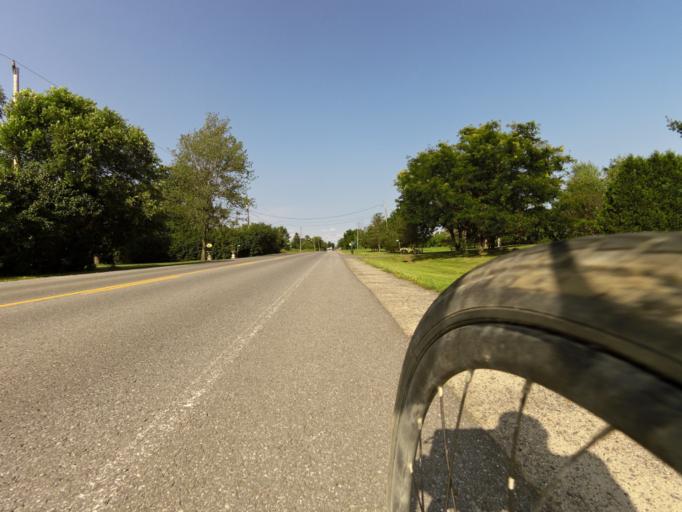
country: CA
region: Ontario
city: Kingston
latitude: 44.2881
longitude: -76.7099
